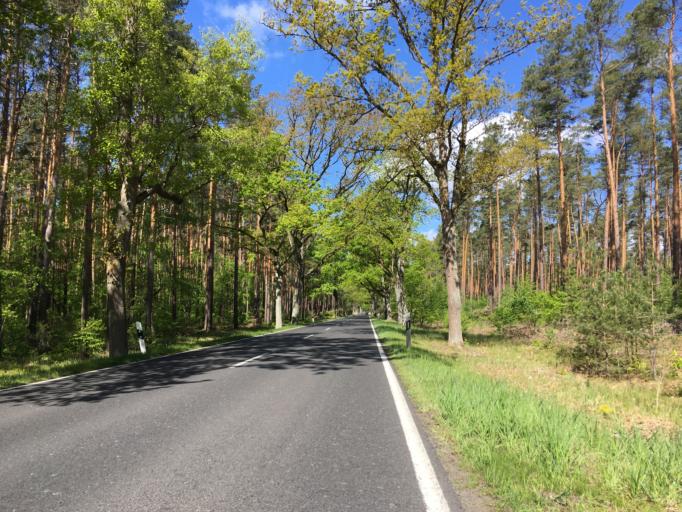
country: DE
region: Brandenburg
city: Birkenwerder
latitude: 52.7219
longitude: 13.3285
